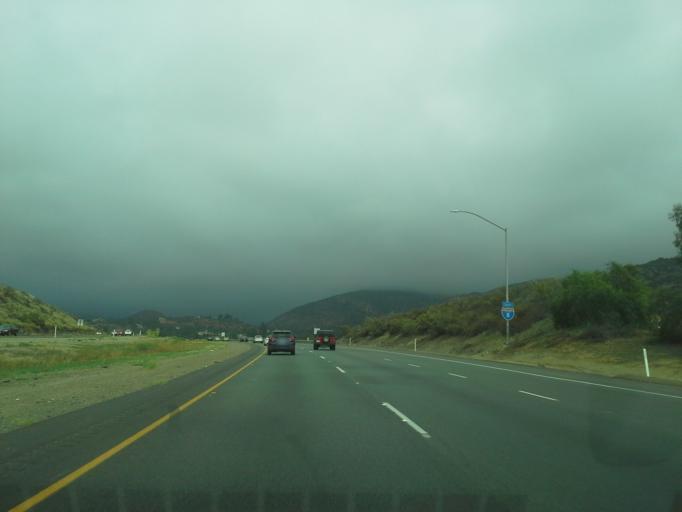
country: US
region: California
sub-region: San Diego County
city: Crest
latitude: 32.8452
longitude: -116.8785
